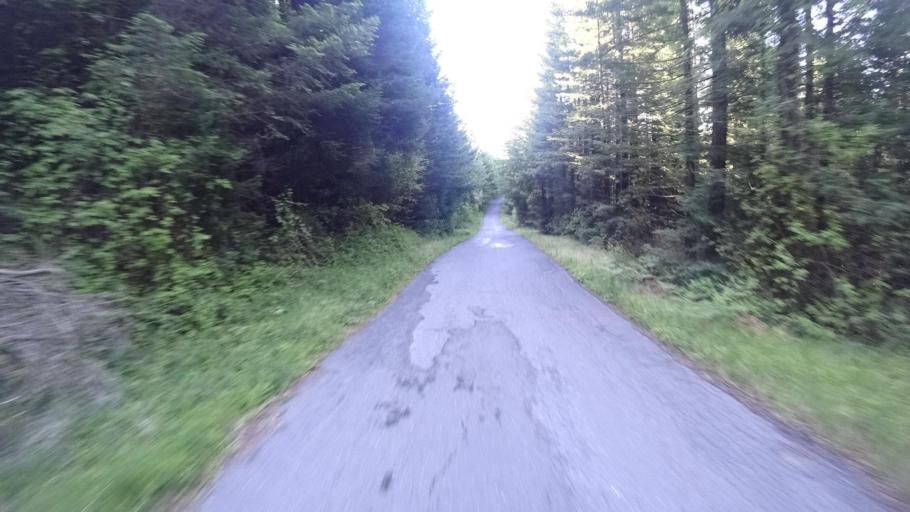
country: US
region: California
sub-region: Humboldt County
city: Rio Dell
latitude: 40.4479
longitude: -123.9771
